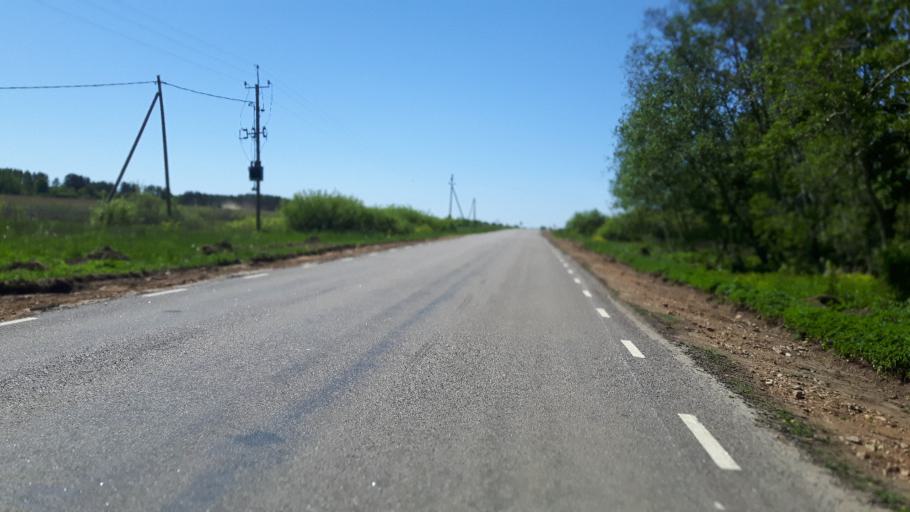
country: EE
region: Ida-Virumaa
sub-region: Narva-Joesuu linn
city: Narva-Joesuu
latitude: 59.4037
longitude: 27.9385
